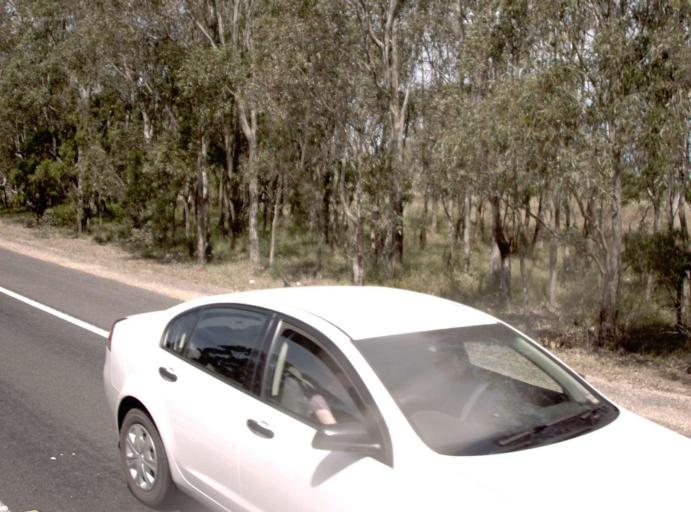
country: AU
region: Victoria
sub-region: East Gippsland
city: Bairnsdale
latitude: -37.8990
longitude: 147.3602
